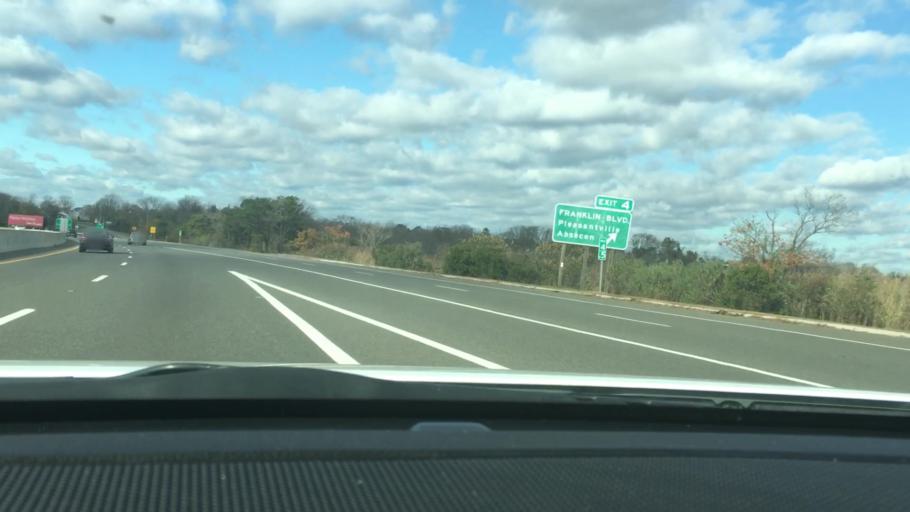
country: US
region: New Jersey
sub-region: Atlantic County
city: Pleasantville
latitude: 39.3937
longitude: -74.5113
